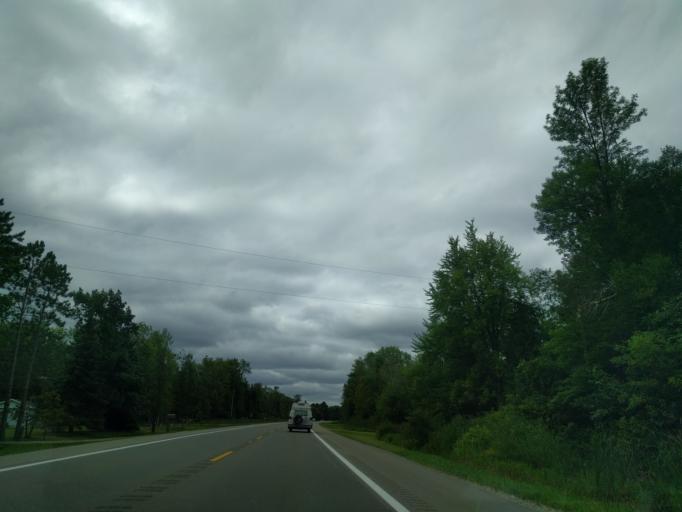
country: US
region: Michigan
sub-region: Menominee County
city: Menominee
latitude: 45.2235
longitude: -87.5143
